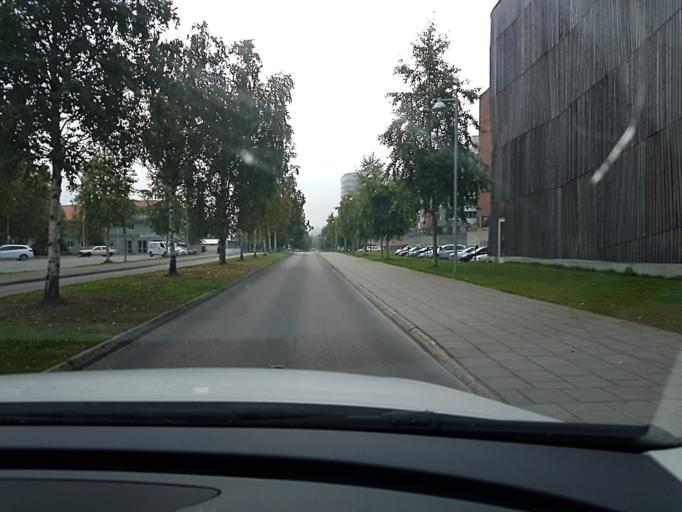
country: SE
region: Norrbotten
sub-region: Pitea Kommun
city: Pitea
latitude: 65.3175
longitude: 21.4836
